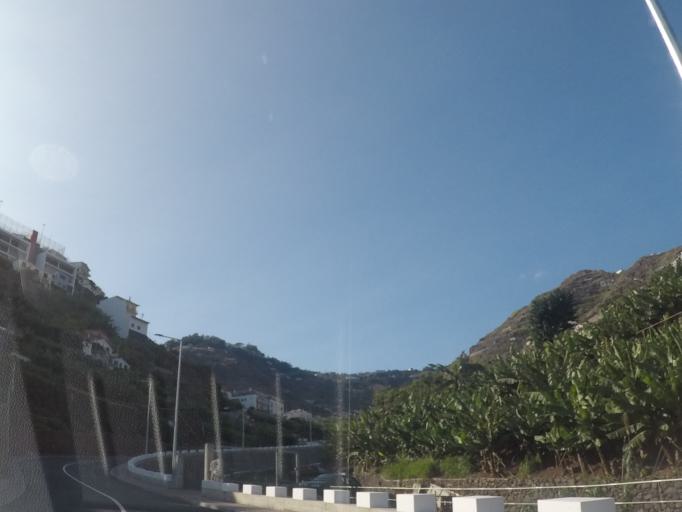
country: PT
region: Madeira
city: Camara de Lobos
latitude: 32.6555
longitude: -16.9882
